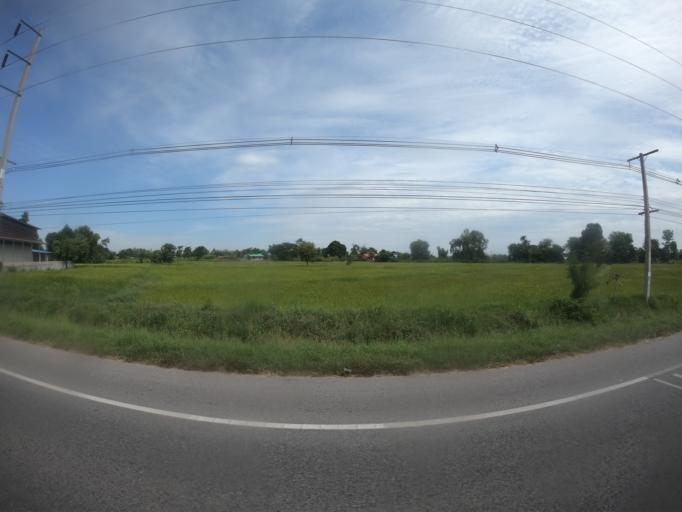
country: TH
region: Maha Sarakham
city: Chiang Yuen
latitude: 16.4239
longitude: 103.0705
